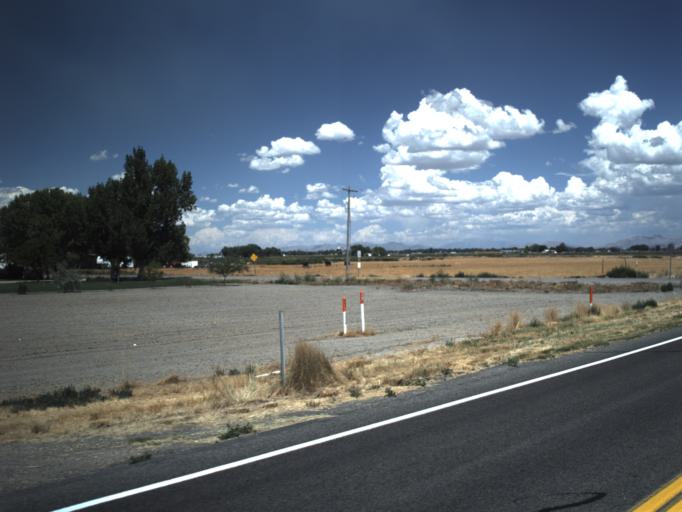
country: US
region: Utah
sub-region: Millard County
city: Delta
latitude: 39.3305
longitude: -112.6156
